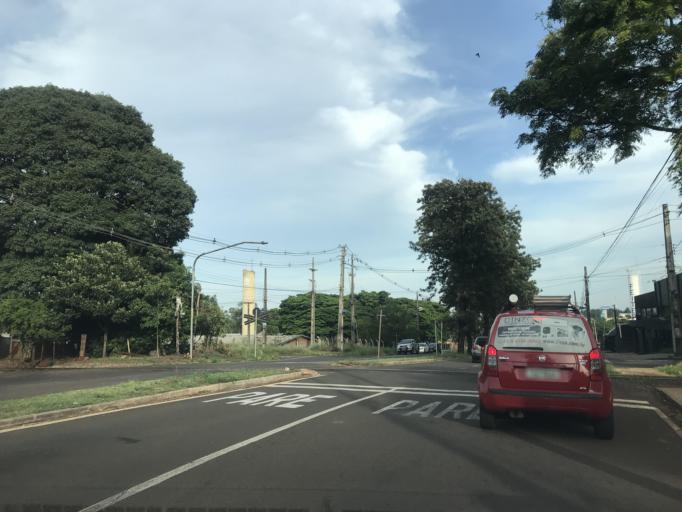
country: BR
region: Parana
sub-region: Maringa
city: Maringa
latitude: -23.4248
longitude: -51.9699
